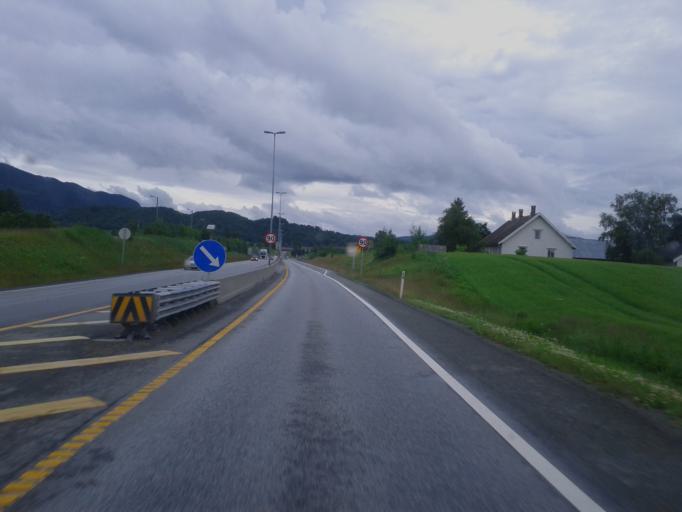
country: NO
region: Sor-Trondelag
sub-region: Melhus
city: Melhus
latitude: 63.3058
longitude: 10.2889
